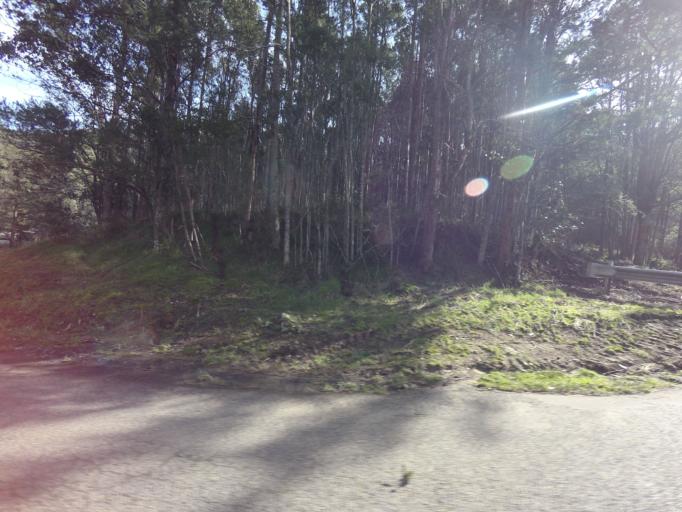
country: AU
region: Tasmania
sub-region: Huon Valley
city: Huonville
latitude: -43.0352
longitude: 147.1438
